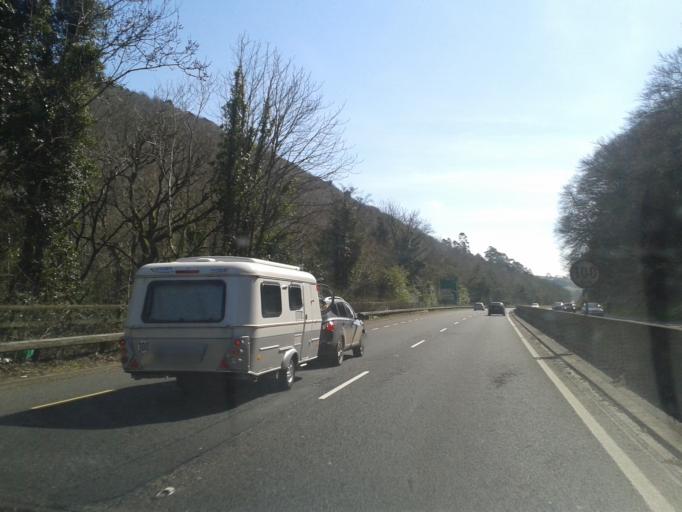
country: IE
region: Leinster
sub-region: Wicklow
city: Kilmacanoge
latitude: 53.1384
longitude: -6.1198
